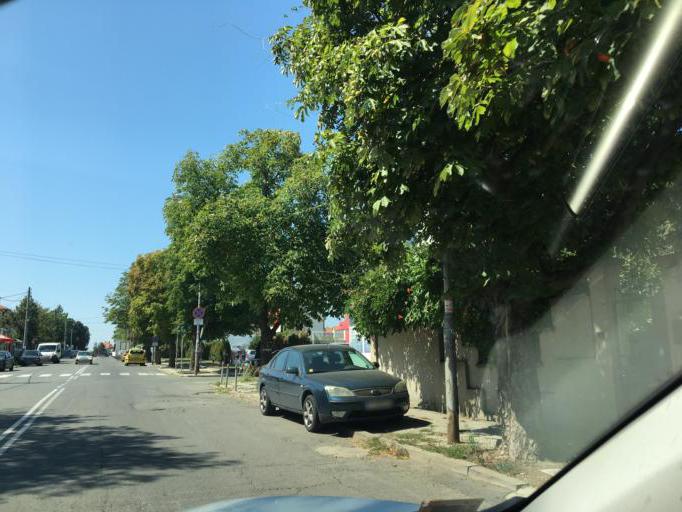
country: BG
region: Burgas
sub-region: Obshtina Kameno
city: Kameno
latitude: 42.6061
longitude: 27.3868
